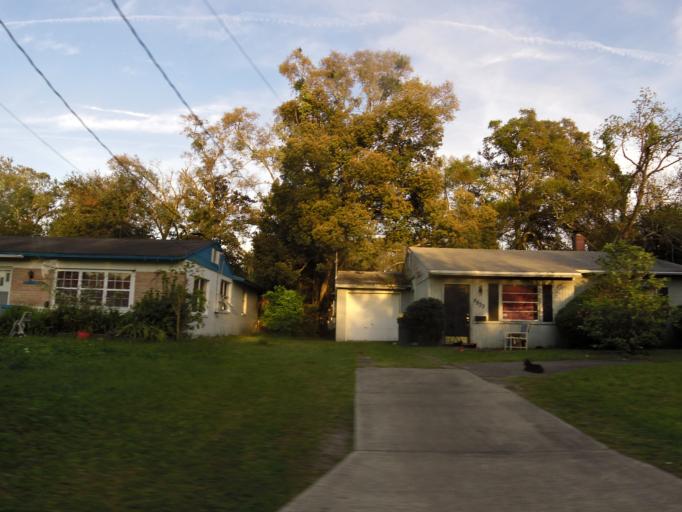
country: US
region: Florida
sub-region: Duval County
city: Jacksonville
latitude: 30.2956
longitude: -81.6370
